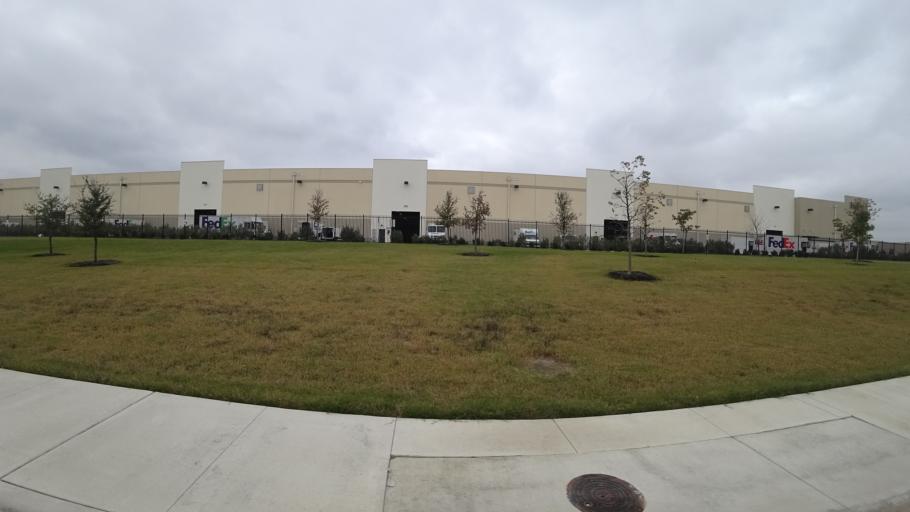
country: US
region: Texas
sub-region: Travis County
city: Pflugerville
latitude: 30.4175
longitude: -97.5905
